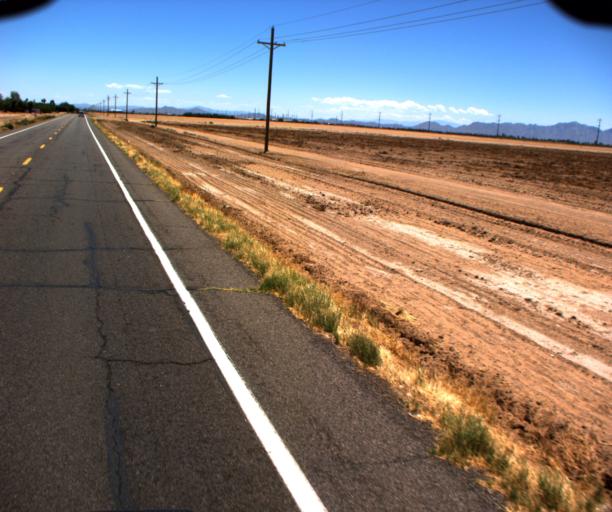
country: US
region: Arizona
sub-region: Pinal County
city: Coolidge
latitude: 32.8797
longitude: -111.5957
